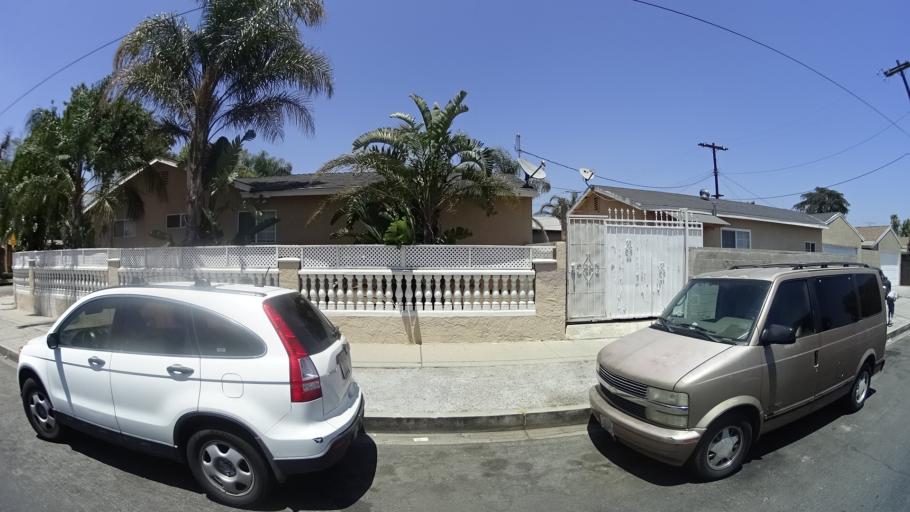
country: US
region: California
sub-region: Los Angeles County
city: Van Nuys
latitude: 34.2246
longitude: -118.4619
